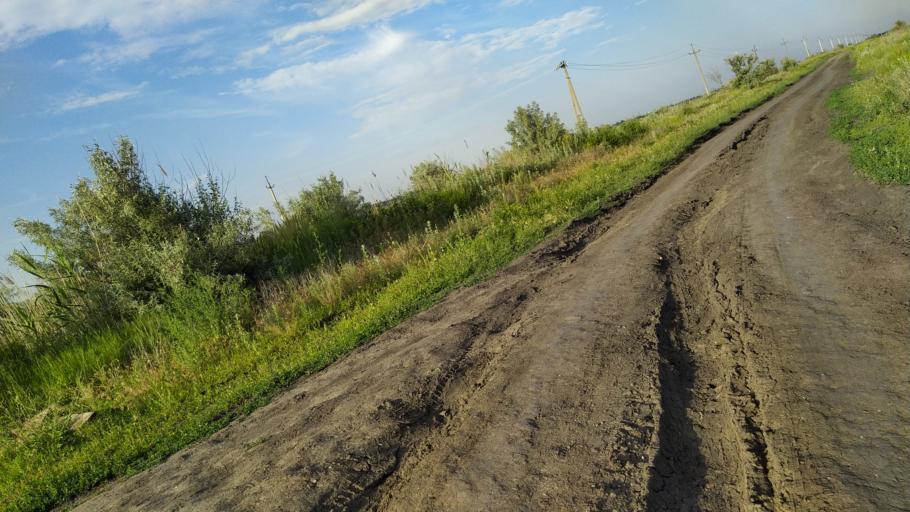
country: RU
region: Rostov
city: Kuleshovka
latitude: 47.1382
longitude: 39.6430
